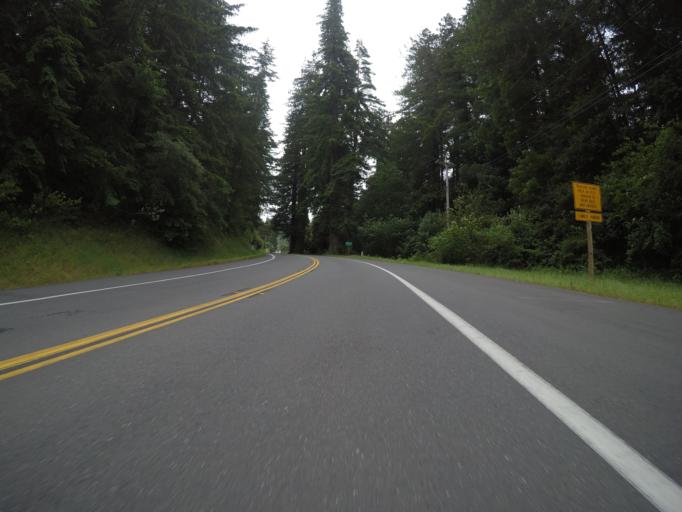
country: US
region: California
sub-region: Humboldt County
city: Rio Dell
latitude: 40.4030
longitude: -123.9512
